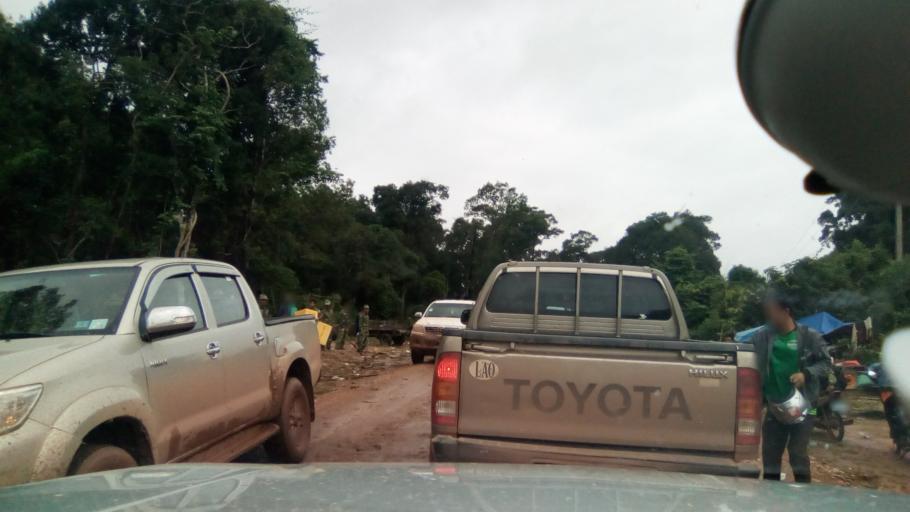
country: LA
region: Attapu
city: Attapu
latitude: 14.6762
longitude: 106.5610
